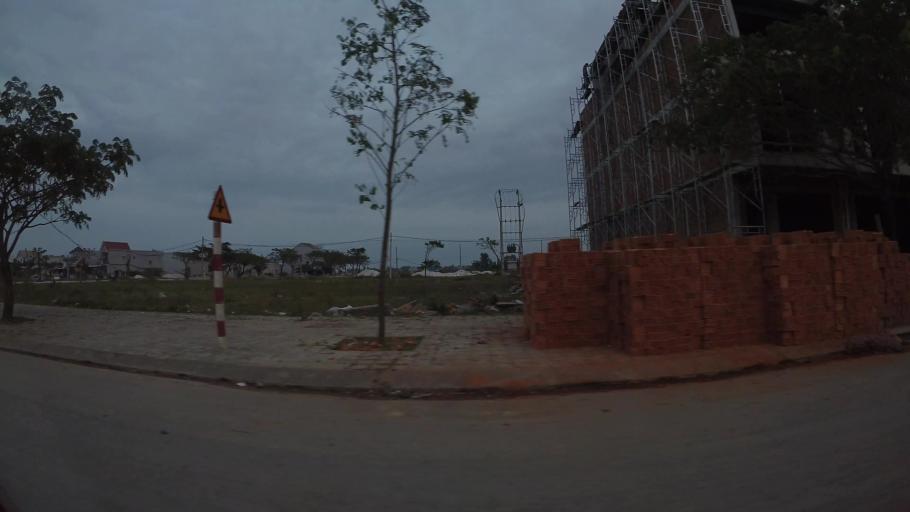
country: VN
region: Da Nang
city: Lien Chieu
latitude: 16.0998
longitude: 108.1159
